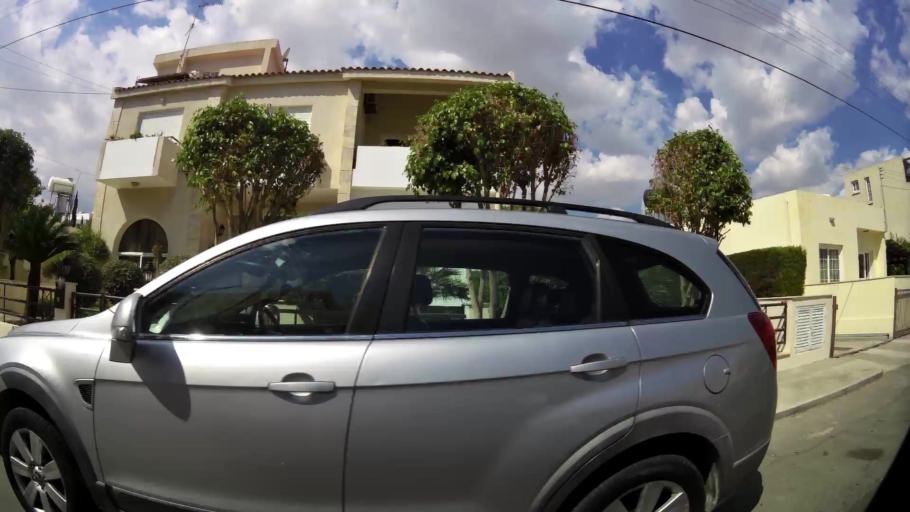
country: CY
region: Larnaka
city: Larnaca
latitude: 34.9123
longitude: 33.6129
